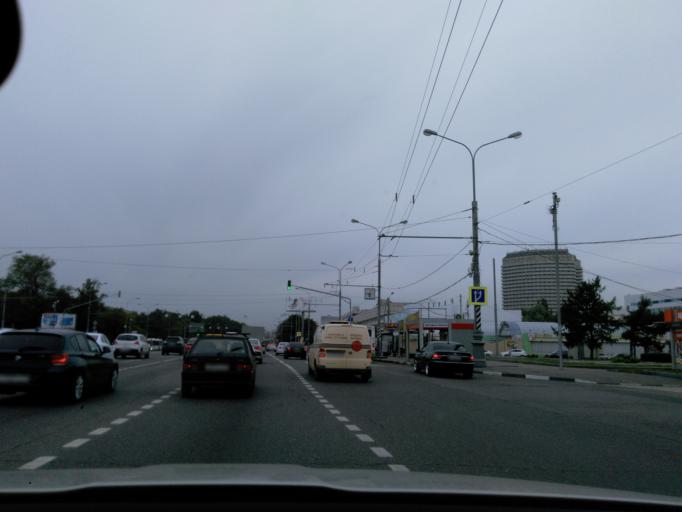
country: RU
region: Moscow
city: Tsaritsyno
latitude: 55.6549
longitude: 37.6497
